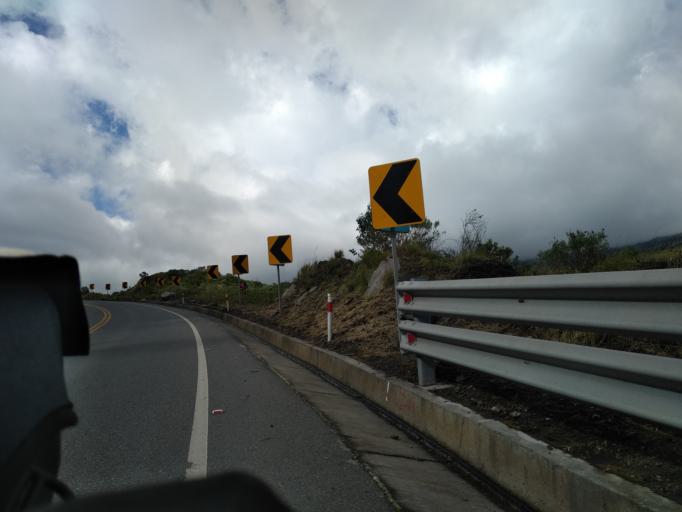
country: EC
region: Tungurahua
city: Banos
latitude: -1.4928
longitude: -78.5181
